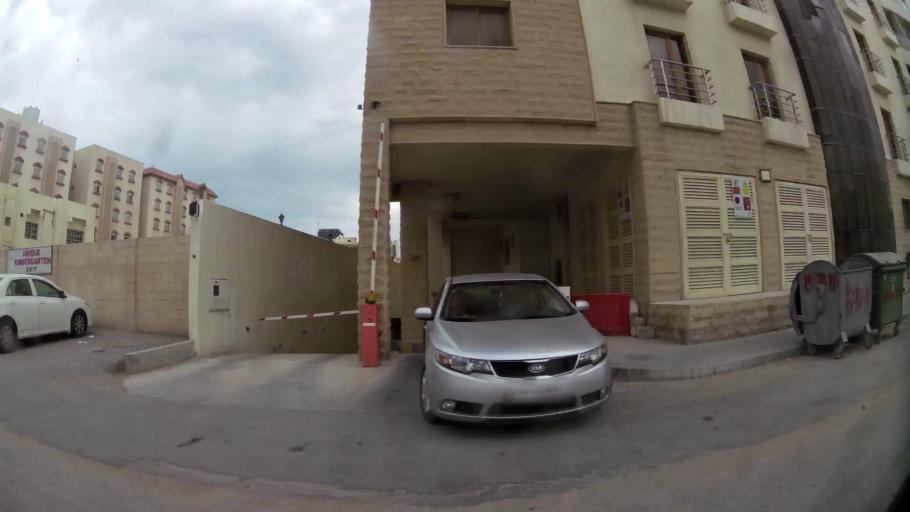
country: QA
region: Baladiyat ad Dawhah
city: Doha
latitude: 25.2784
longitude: 51.5000
